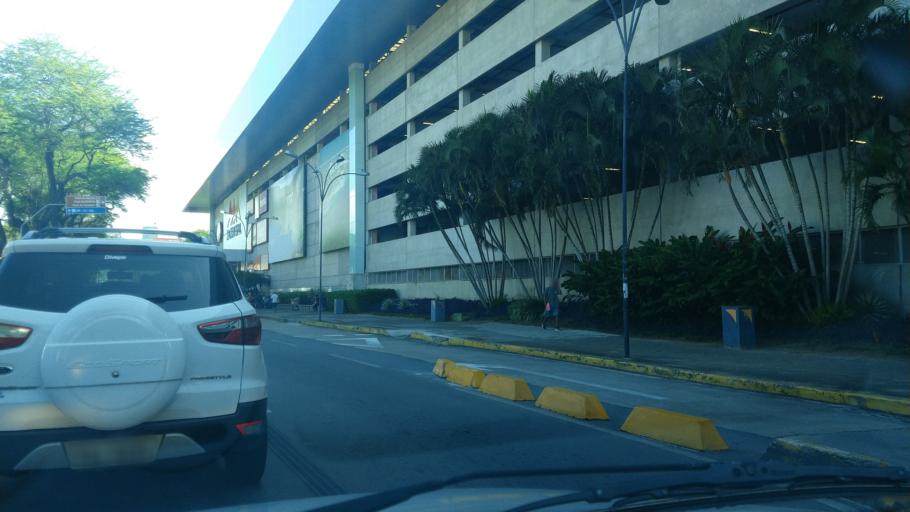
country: BR
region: Rio Grande do Norte
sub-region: Natal
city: Natal
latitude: -5.8113
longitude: -35.2046
